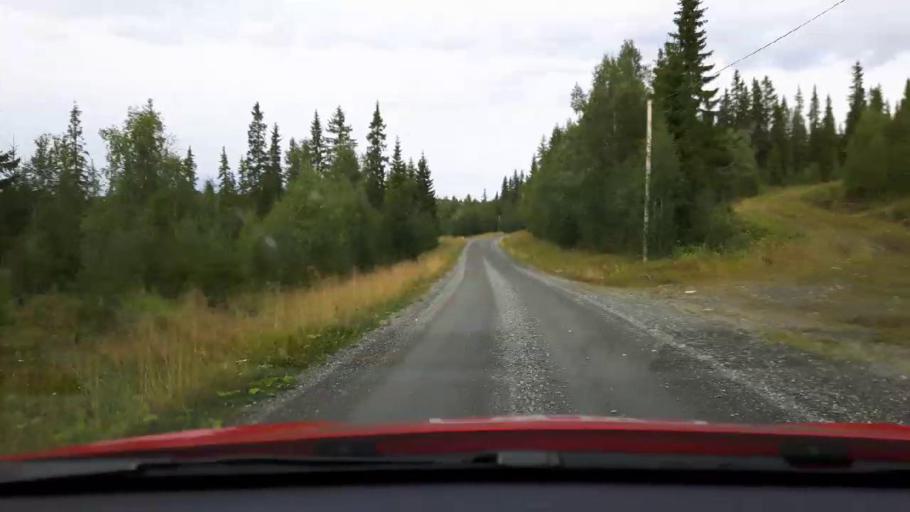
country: SE
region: Jaemtland
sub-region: Are Kommun
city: Are
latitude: 63.7660
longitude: 13.0937
